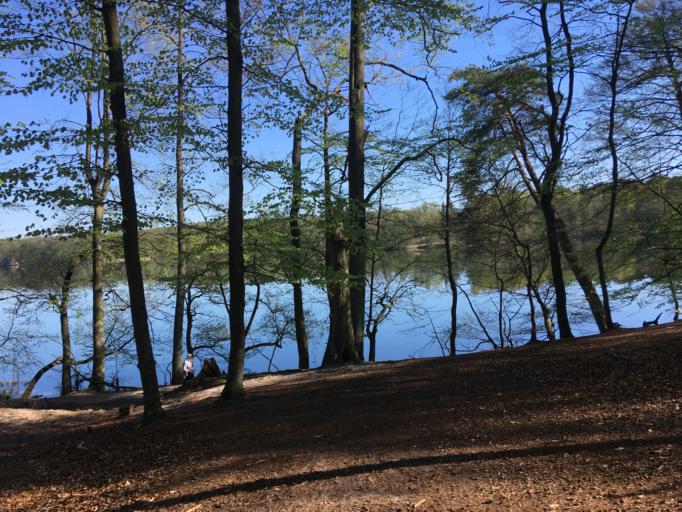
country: DE
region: Brandenburg
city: Wandlitz
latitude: 52.7405
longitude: 13.4968
